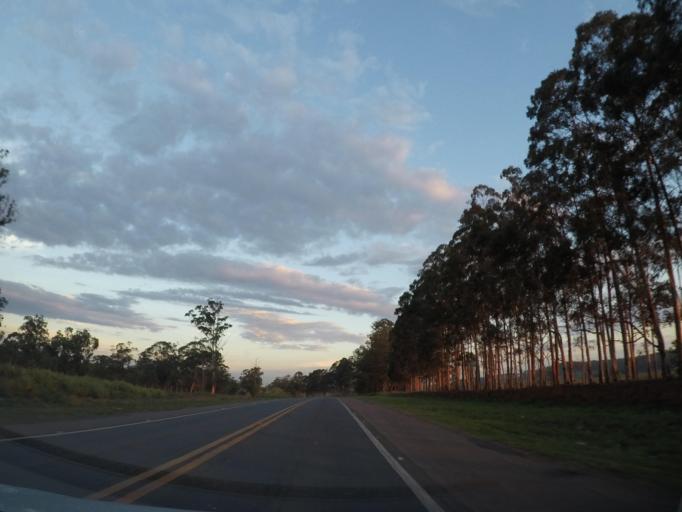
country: BR
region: Sao Paulo
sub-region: Itupeva
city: Itupeva
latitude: -23.0481
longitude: -47.0913
